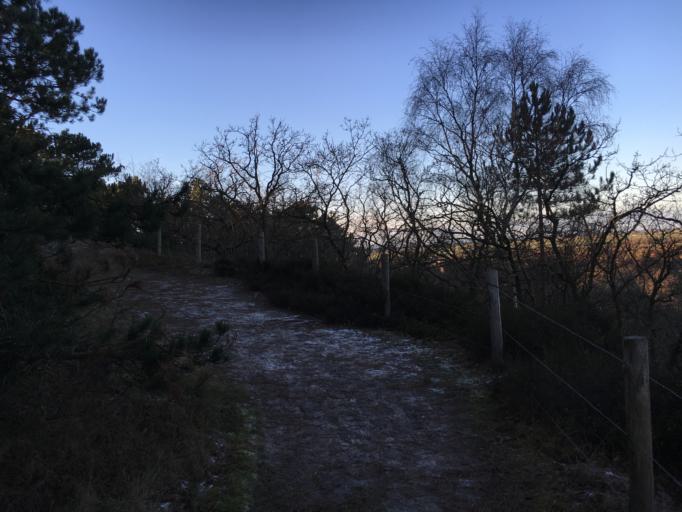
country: NL
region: North Holland
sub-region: Gemeente Bergen
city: Egmond aan Zee
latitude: 52.7174
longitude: 4.6711
